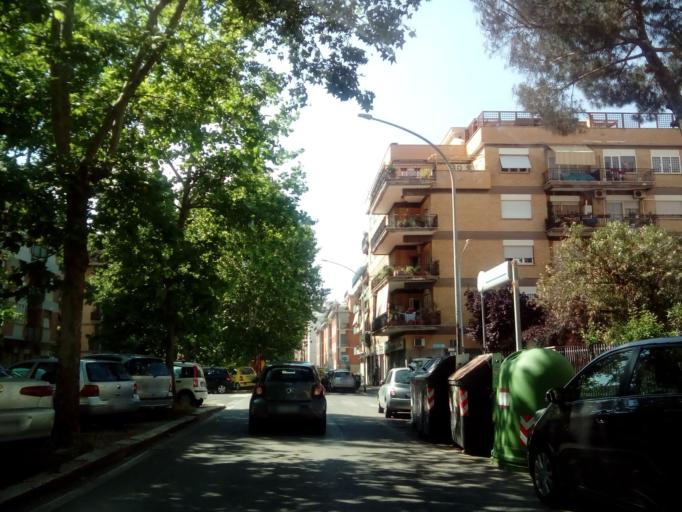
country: IT
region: Latium
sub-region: Citta metropolitana di Roma Capitale
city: Rome
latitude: 41.8552
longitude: 12.5600
